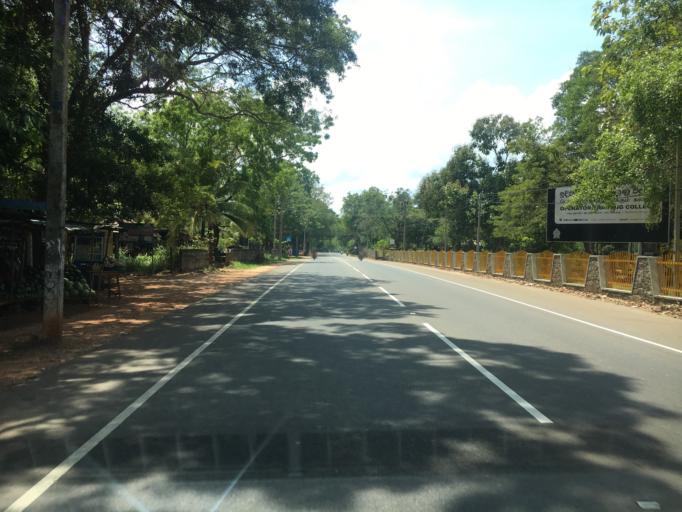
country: LK
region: North Central
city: Anuradhapura
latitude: 8.2682
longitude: 80.5037
